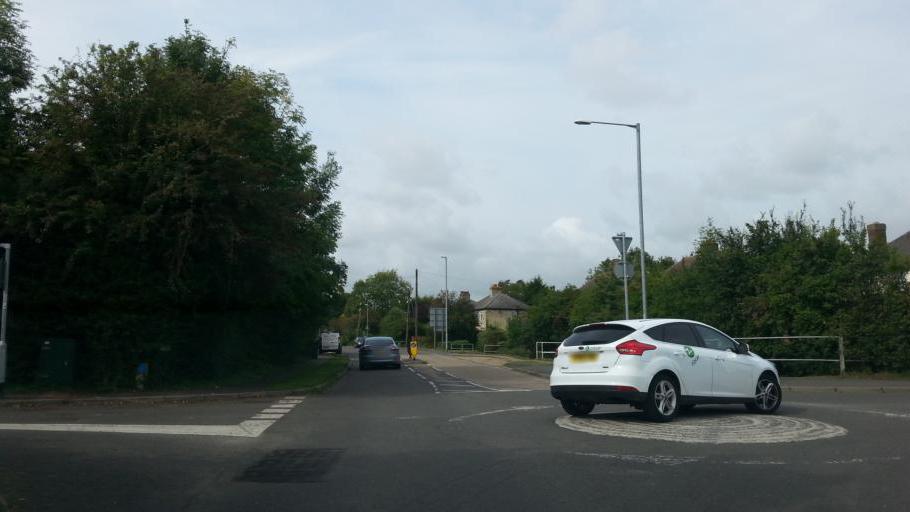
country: GB
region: England
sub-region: Cambridgeshire
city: Comberton
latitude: 52.1882
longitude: 0.0299
